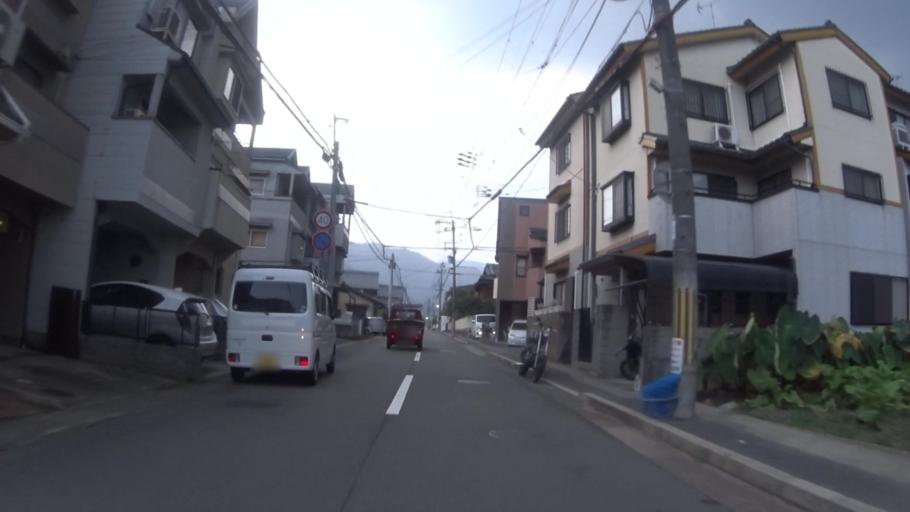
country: JP
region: Kyoto
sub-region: Kyoto-shi
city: Kamigyo-ku
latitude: 35.0706
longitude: 135.7455
